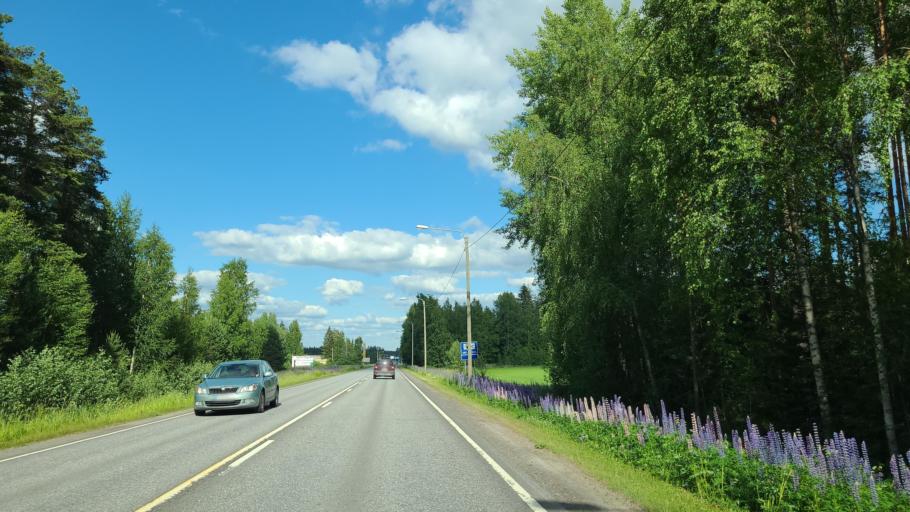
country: FI
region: Southern Ostrobothnia
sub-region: Kuusiokunnat
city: Alavus
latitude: 62.5902
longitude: 23.5926
